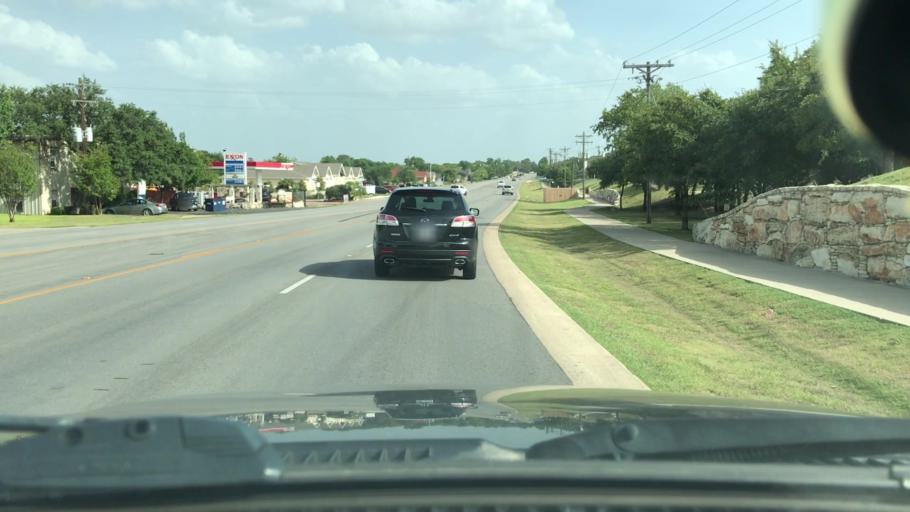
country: US
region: Texas
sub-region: Williamson County
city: Leander
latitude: 30.5499
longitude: -97.8537
